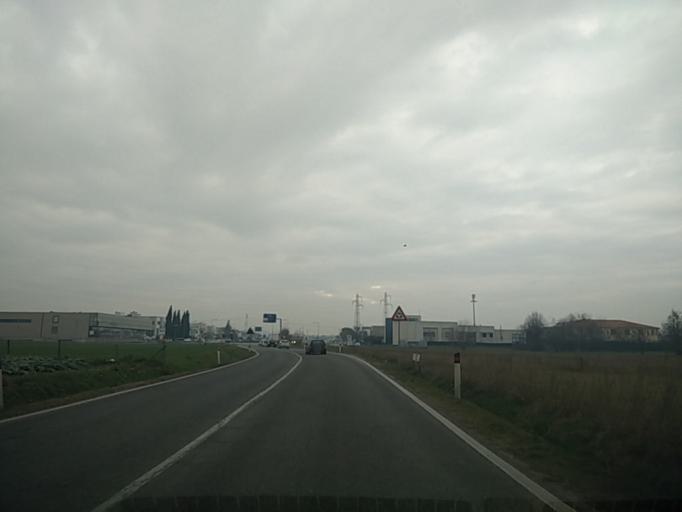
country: IT
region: Emilia-Romagna
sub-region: Provincia di Rimini
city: Santa Giustina
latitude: 44.0680
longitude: 12.4749
